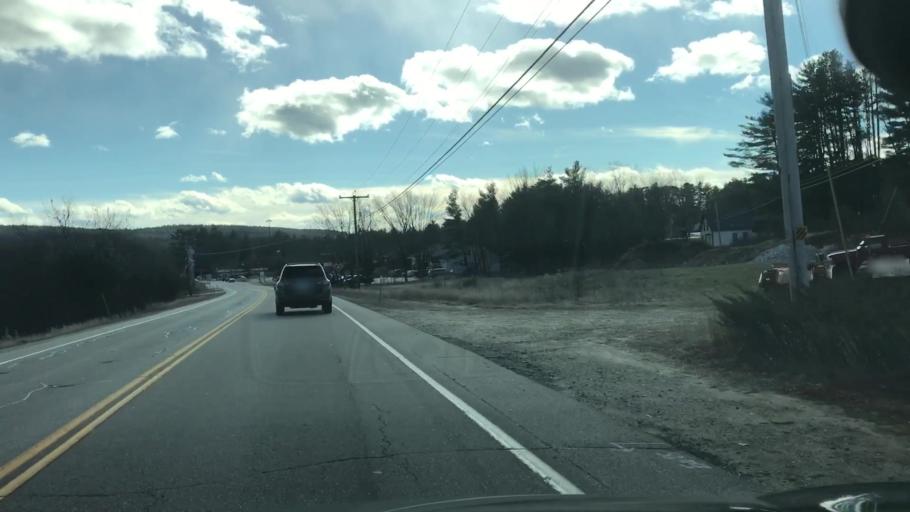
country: US
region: New Hampshire
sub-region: Merrimack County
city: Epsom
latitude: 43.2319
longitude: -71.3613
